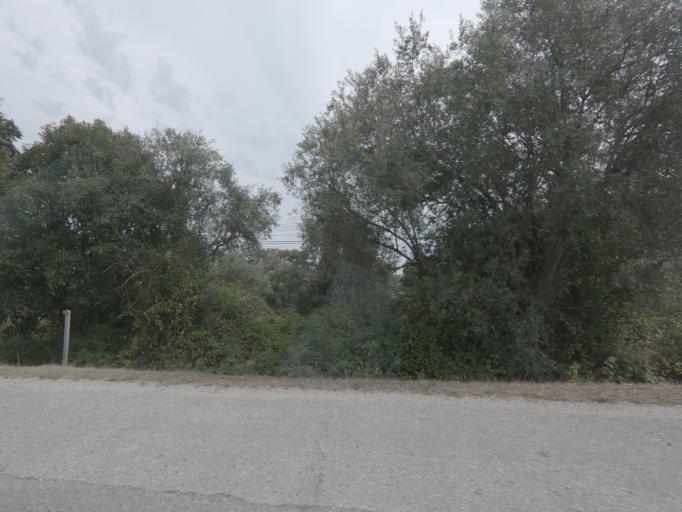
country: PT
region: Leiria
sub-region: Pombal
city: Pombal
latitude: 39.9006
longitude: -8.6384
